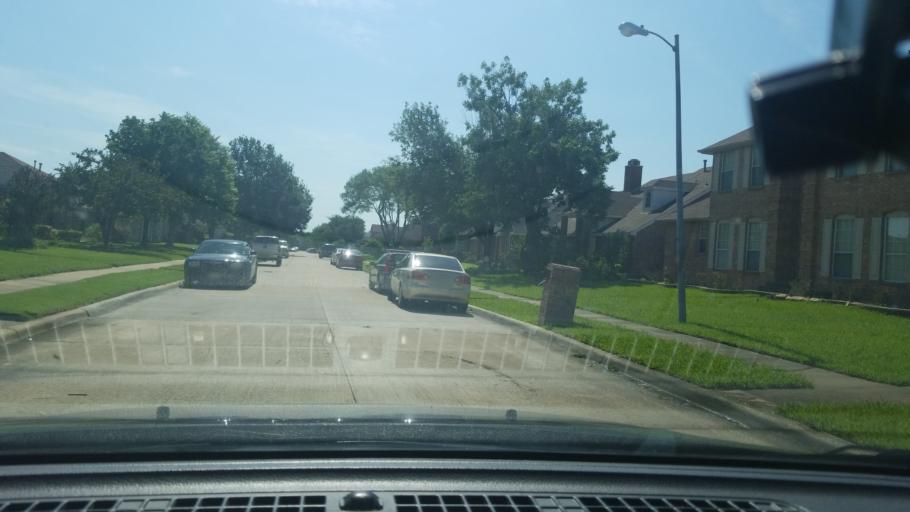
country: US
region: Texas
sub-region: Dallas County
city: Mesquite
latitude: 32.7768
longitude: -96.5872
